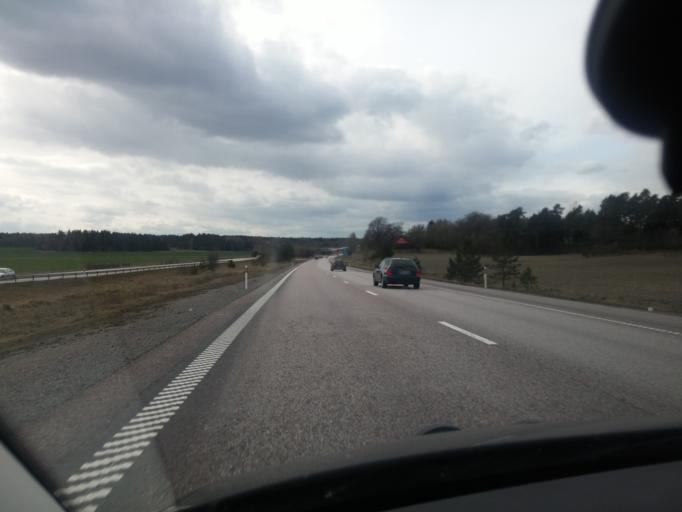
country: SE
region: Uppsala
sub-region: Enkopings Kommun
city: Grillby
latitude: 59.6331
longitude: 17.2975
